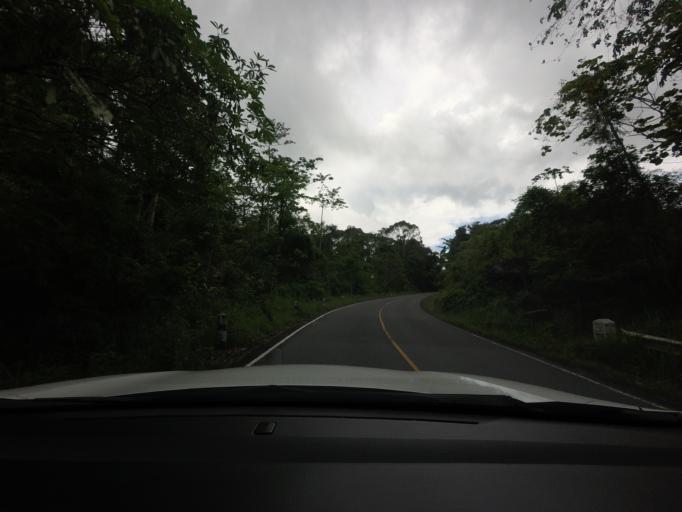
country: TH
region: Nakhon Nayok
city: Nakhon Nayok
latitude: 14.3601
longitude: 101.3452
